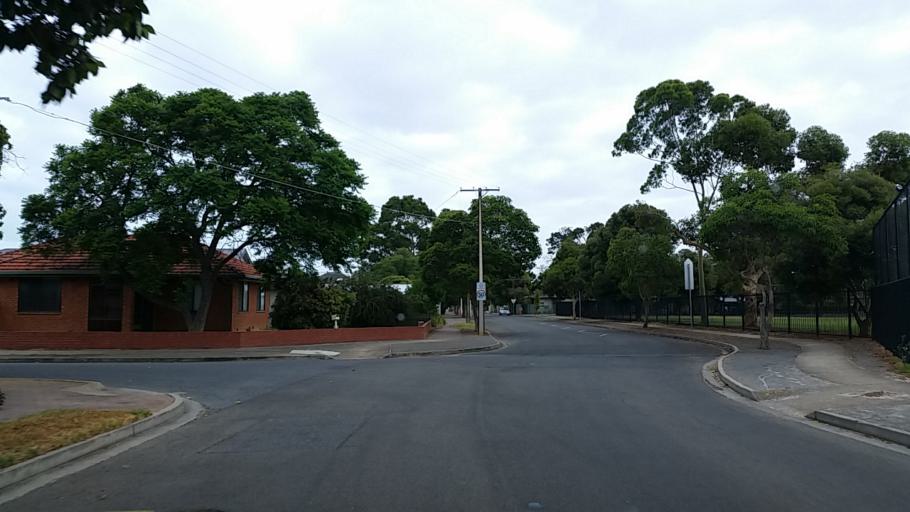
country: AU
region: South Australia
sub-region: Holdfast Bay
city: North Brighton
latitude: -35.0030
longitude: 138.5246
